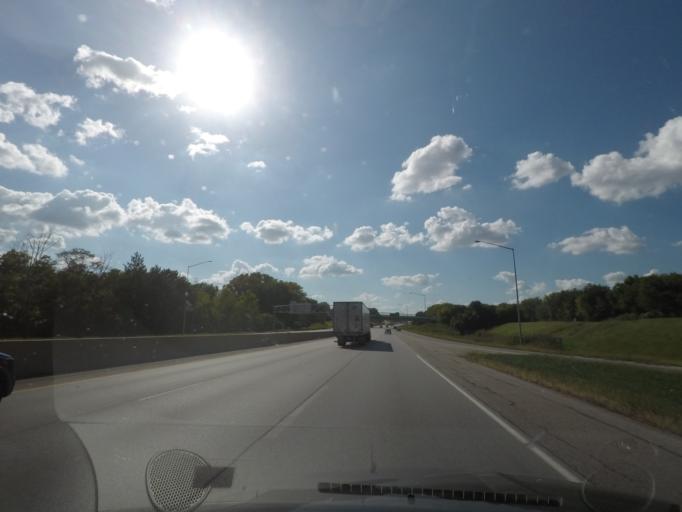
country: US
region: Iowa
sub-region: Polk County
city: Clive
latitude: 41.5926
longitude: -93.7393
